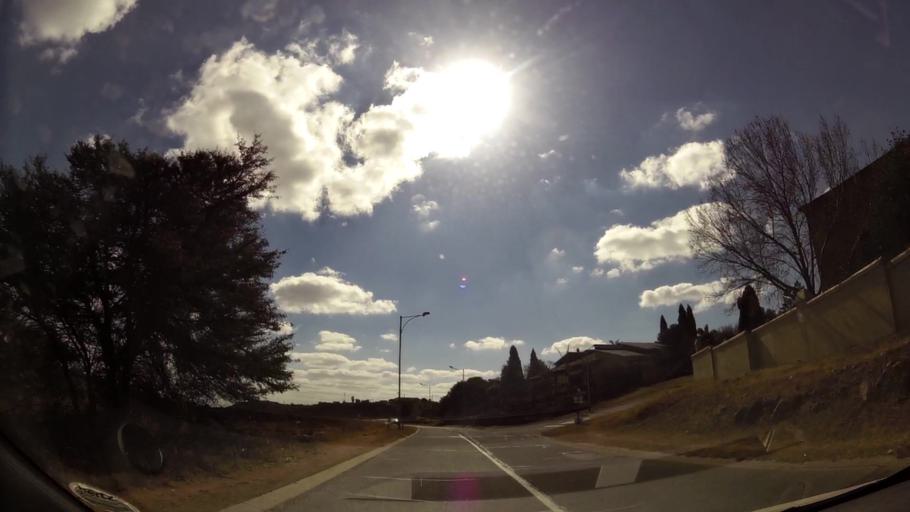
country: ZA
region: Gauteng
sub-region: West Rand District Municipality
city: Krugersdorp
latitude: -26.0913
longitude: 27.8030
